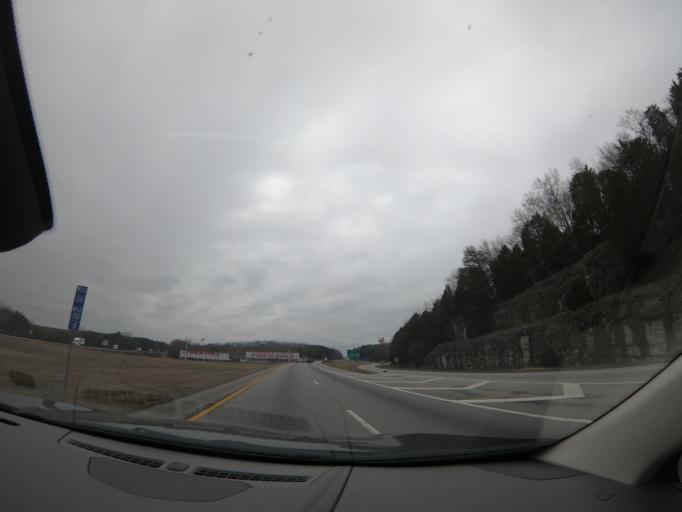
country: US
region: Tennessee
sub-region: Marion County
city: Jasper
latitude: 35.0318
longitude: -85.5787
